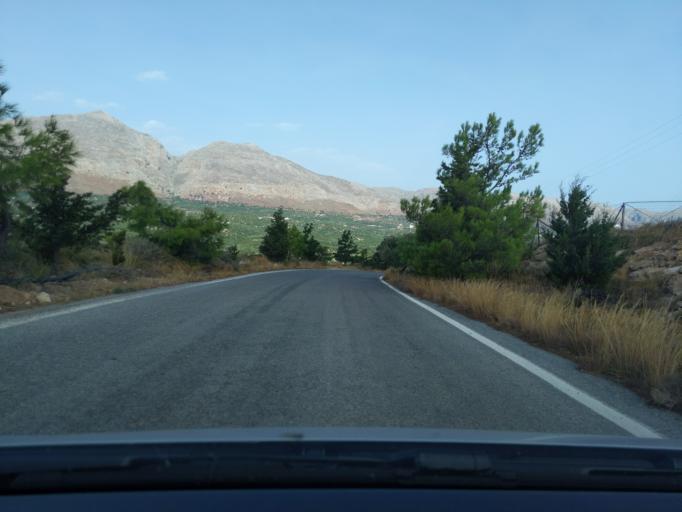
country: GR
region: Crete
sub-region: Nomos Lasithiou
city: Palekastro
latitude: 35.0929
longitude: 26.2354
